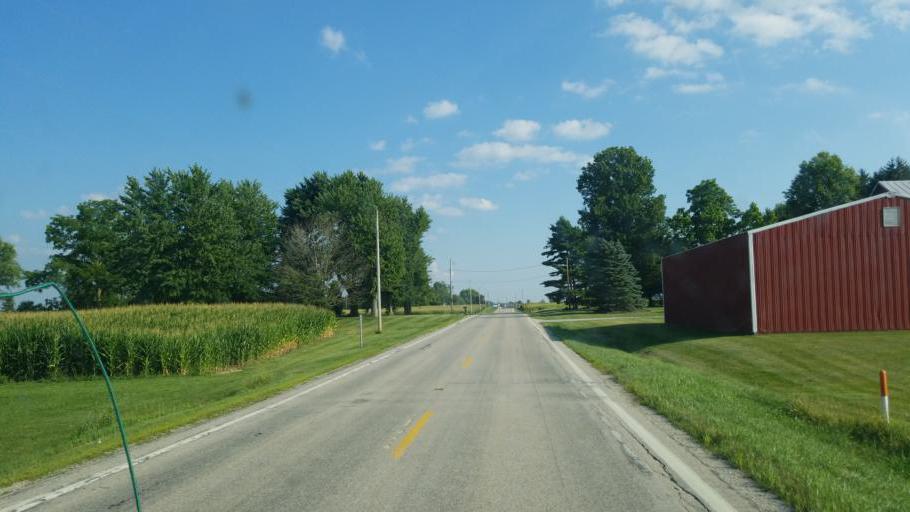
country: US
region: Ohio
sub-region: Crawford County
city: Bucyrus
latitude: 40.8814
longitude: -83.0099
